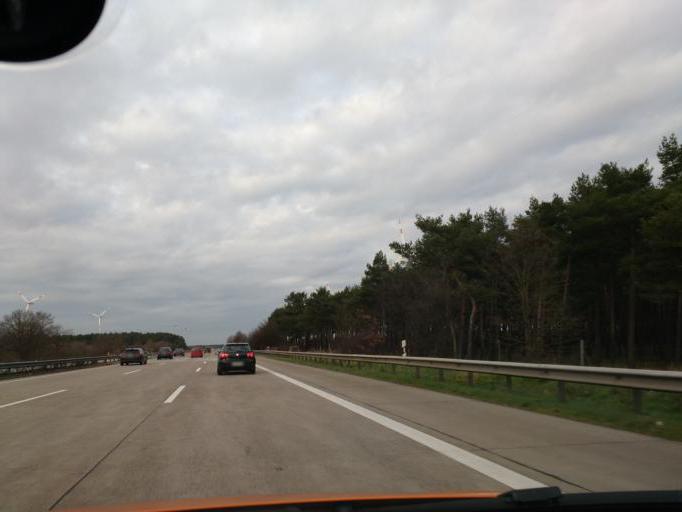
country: DE
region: Lower Saxony
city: Lindwedel
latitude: 52.6370
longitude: 9.7167
